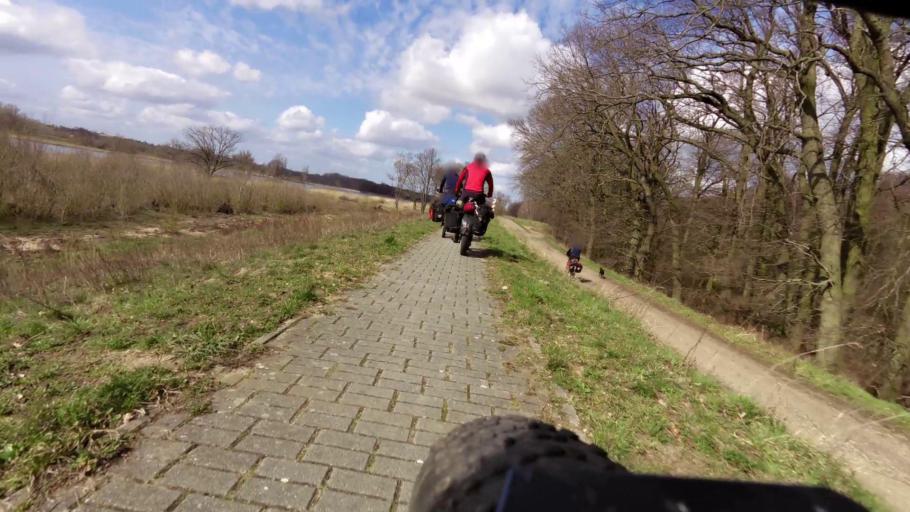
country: PL
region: Lubusz
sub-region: Powiat slubicki
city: Slubice
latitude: 52.3789
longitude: 14.5533
